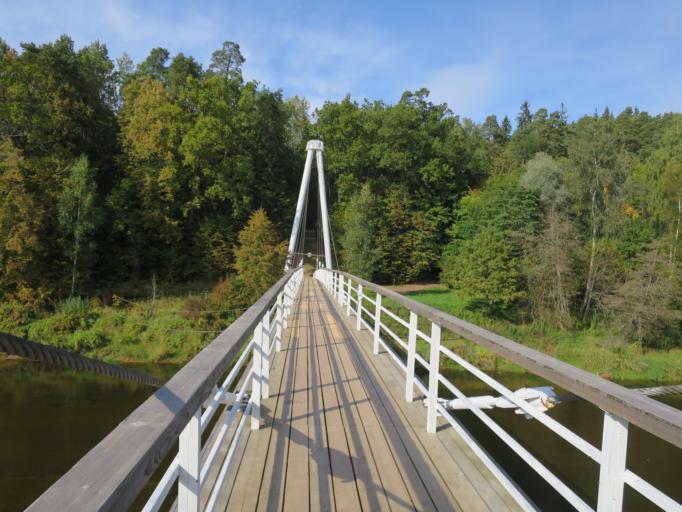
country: LV
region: Sigulda
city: Sigulda
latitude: 57.1491
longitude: 24.8072
